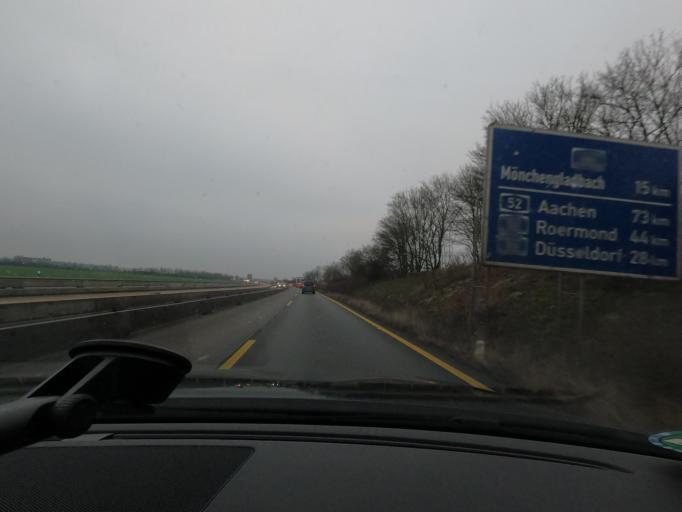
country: DE
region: North Rhine-Westphalia
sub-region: Regierungsbezirk Dusseldorf
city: Willich
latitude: 51.2848
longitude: 6.5160
